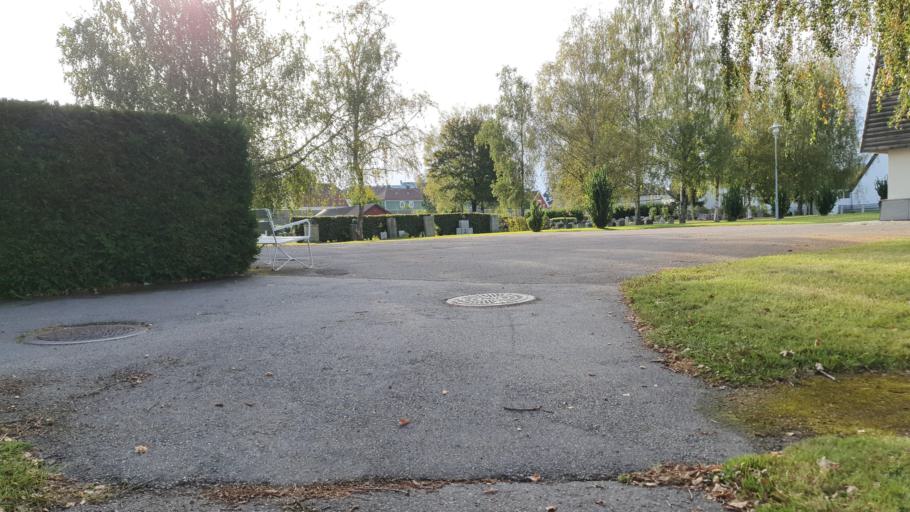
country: NO
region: Vestfold
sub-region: Tonsberg
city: Tonsberg
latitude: 59.2749
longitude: 10.4215
